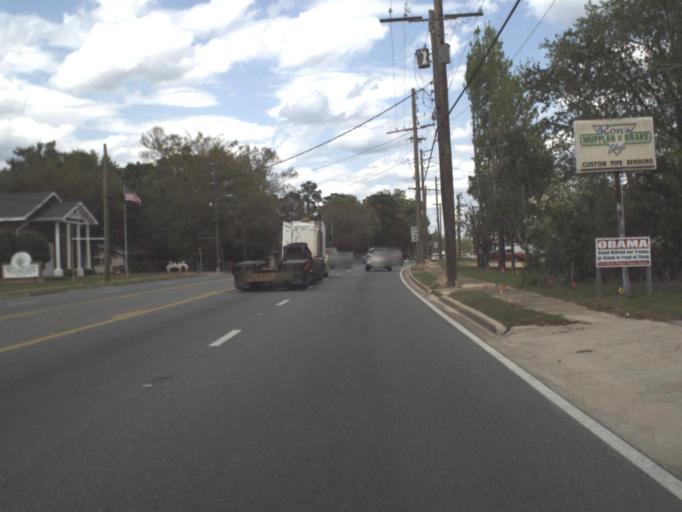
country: US
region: Florida
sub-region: Okaloosa County
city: Crestview
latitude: 30.7743
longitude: -86.5642
